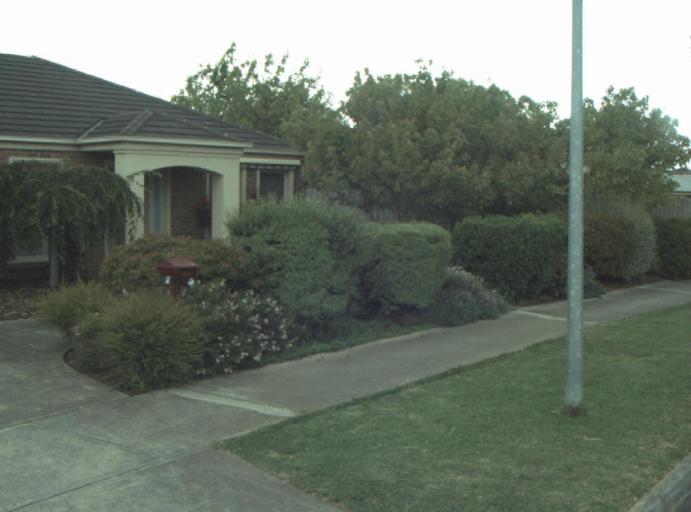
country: AU
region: Victoria
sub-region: Greater Geelong
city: Wandana Heights
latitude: -38.1931
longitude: 144.3214
